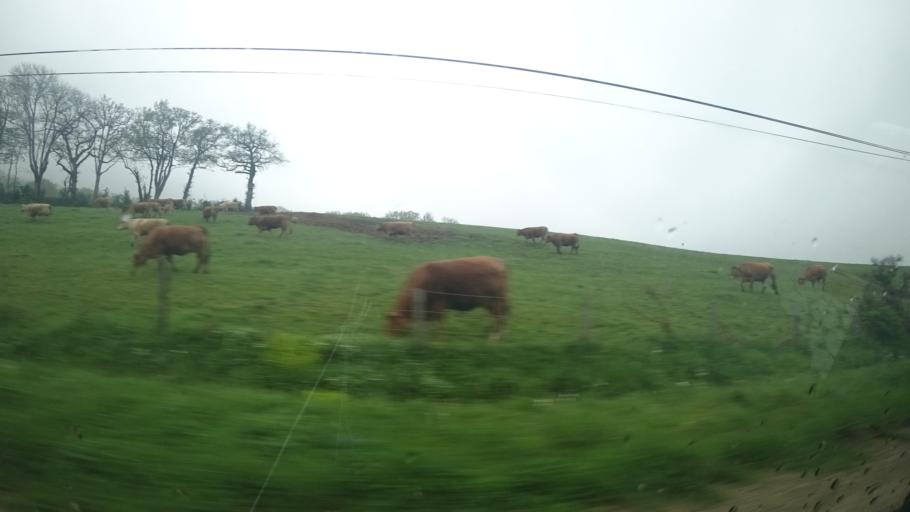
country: FR
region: Midi-Pyrenees
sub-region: Departement de l'Aveyron
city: Laissac
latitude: 44.2835
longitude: 2.8480
